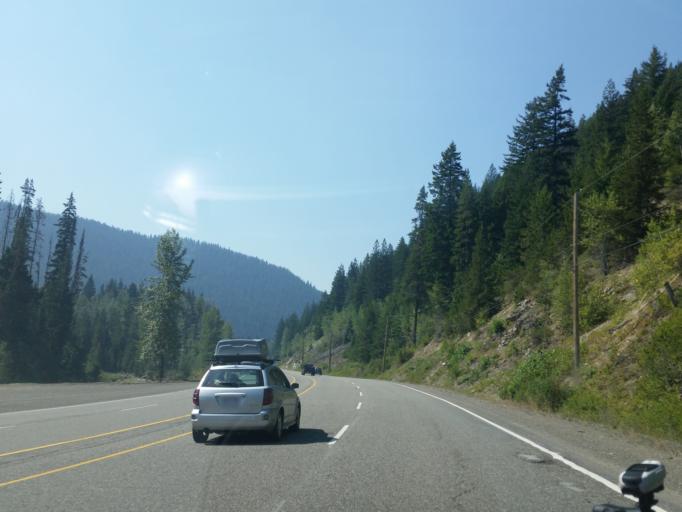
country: CA
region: British Columbia
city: Princeton
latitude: 49.0824
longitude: -120.6944
